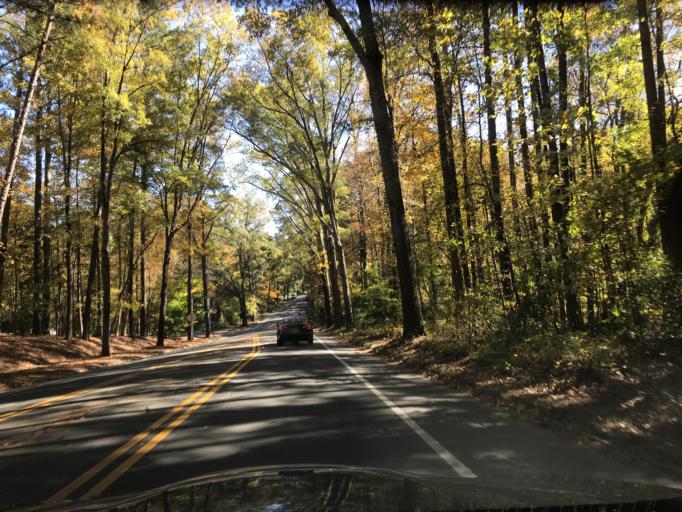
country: US
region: North Carolina
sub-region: Durham County
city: Durham
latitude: 35.9983
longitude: -78.9292
